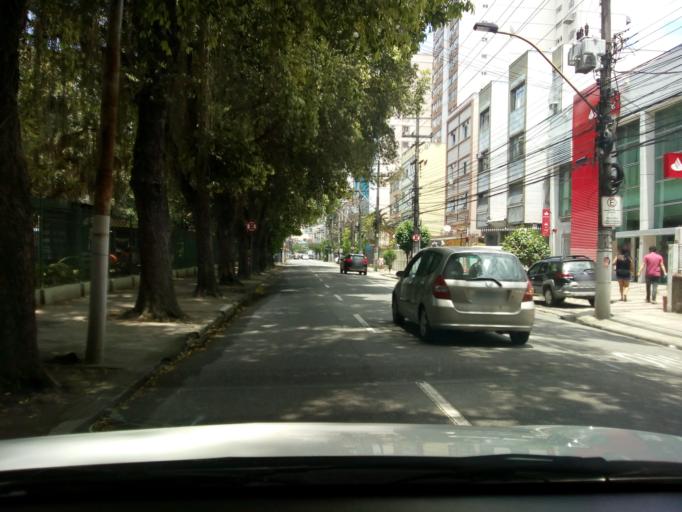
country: BR
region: Rio de Janeiro
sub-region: Niteroi
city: Niteroi
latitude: -22.9054
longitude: -43.1085
